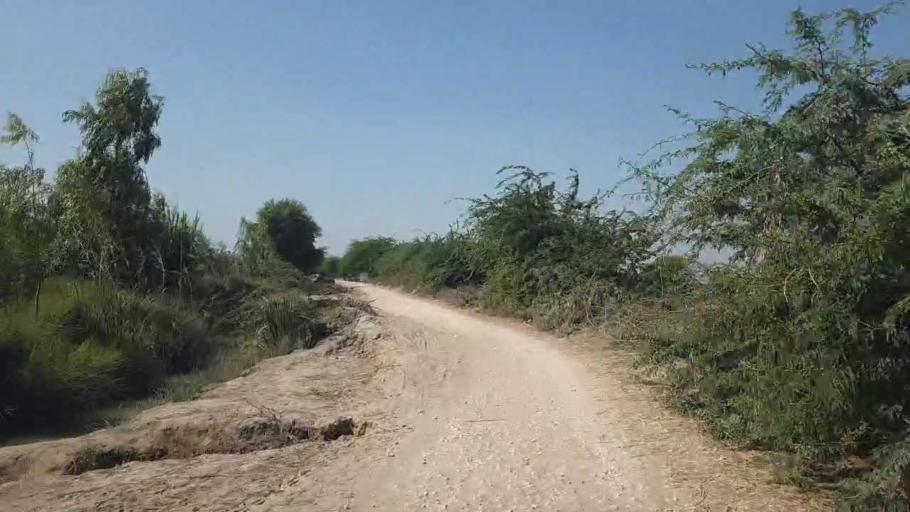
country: PK
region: Sindh
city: Talhar
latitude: 24.8349
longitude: 68.8068
